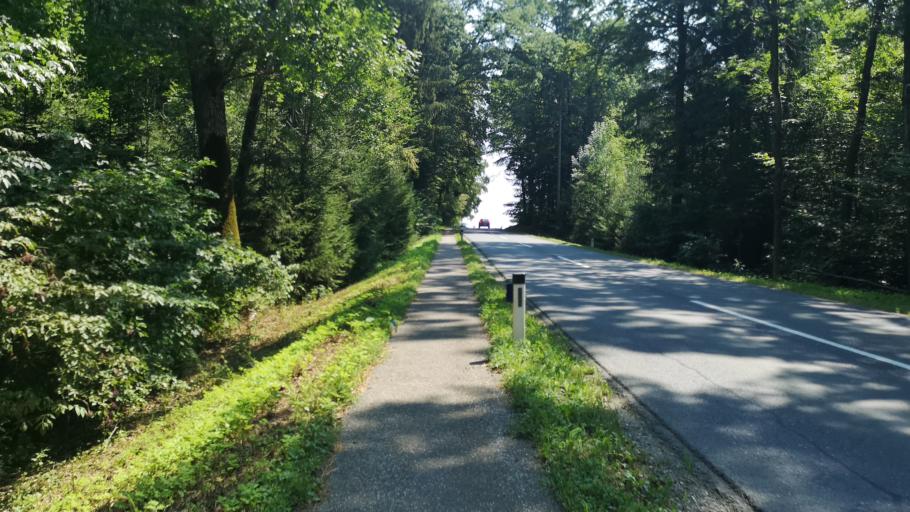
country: AT
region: Styria
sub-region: Politischer Bezirk Deutschlandsberg
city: Preding
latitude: 46.8580
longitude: 15.3914
